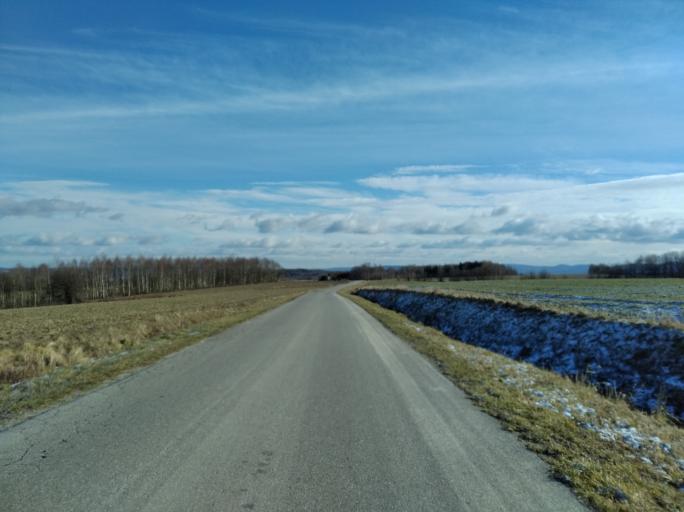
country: PL
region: Subcarpathian Voivodeship
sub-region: Powiat strzyzowski
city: Wisniowa
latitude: 49.9076
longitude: 21.6453
